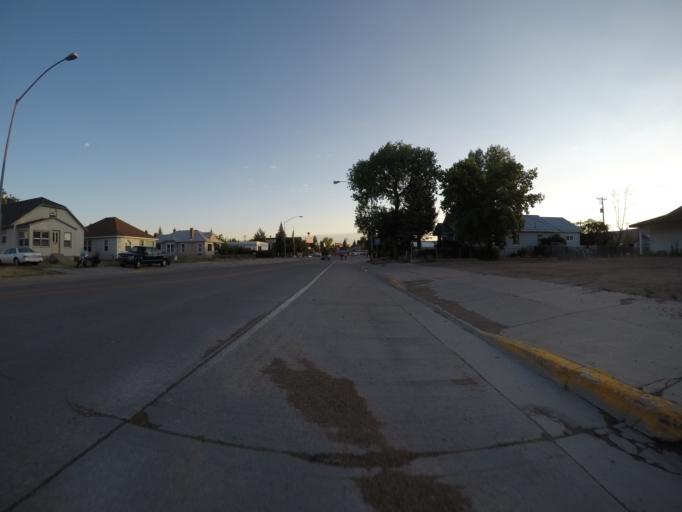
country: US
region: Wyoming
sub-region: Lincoln County
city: Kemmerer
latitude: 41.7880
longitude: -110.5391
